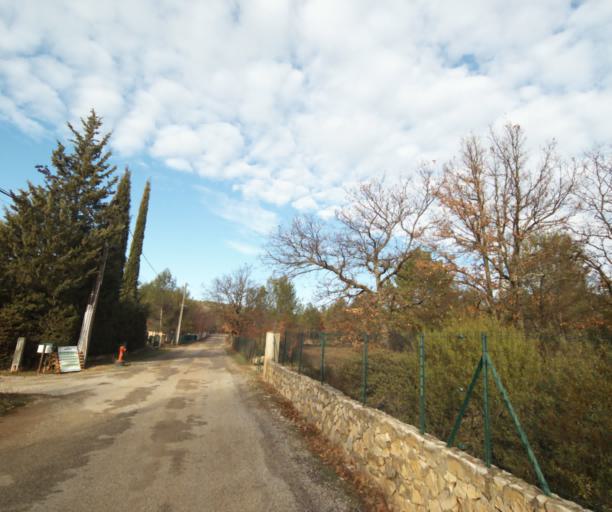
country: FR
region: Provence-Alpes-Cote d'Azur
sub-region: Departement du Var
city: Trans-en-Provence
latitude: 43.4909
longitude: 6.4727
